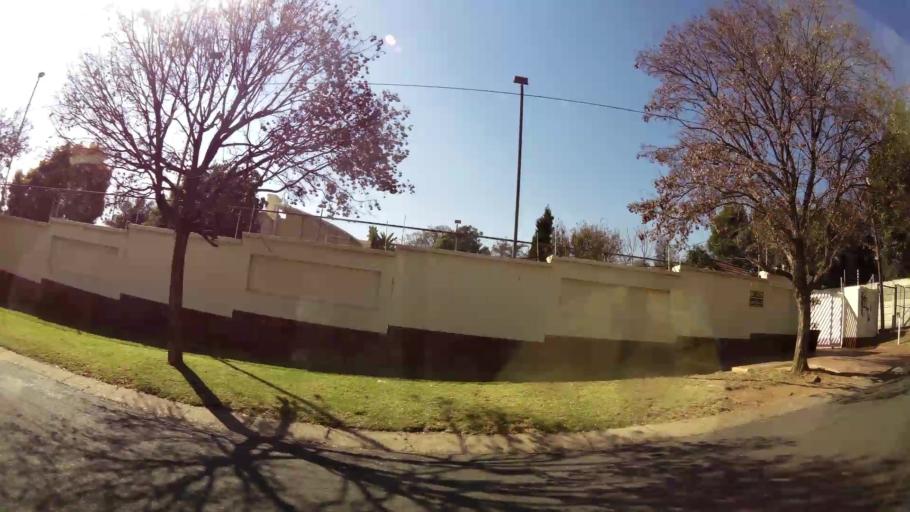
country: ZA
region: Gauteng
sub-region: City of Johannesburg Metropolitan Municipality
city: Modderfontein
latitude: -26.1336
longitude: 28.1085
